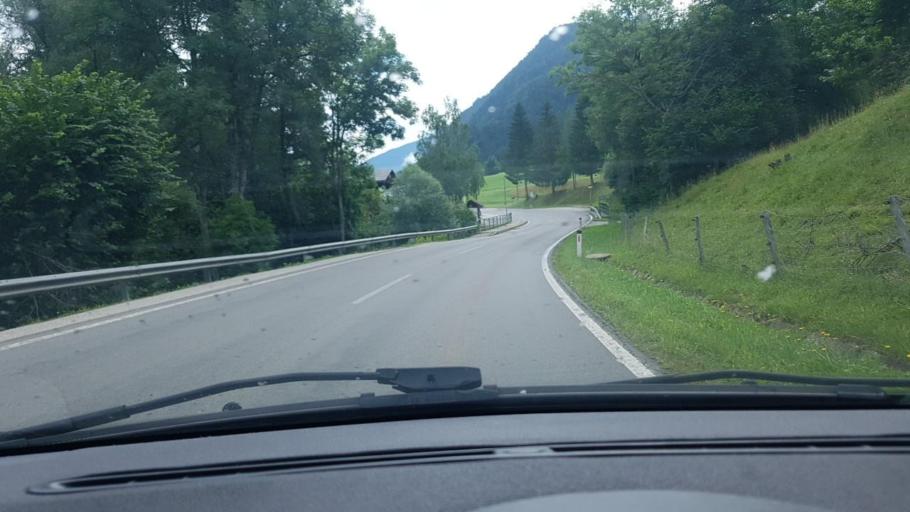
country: AT
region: Carinthia
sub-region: Politischer Bezirk Spittal an der Drau
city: Greifenburg
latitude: 46.7394
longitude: 13.2098
